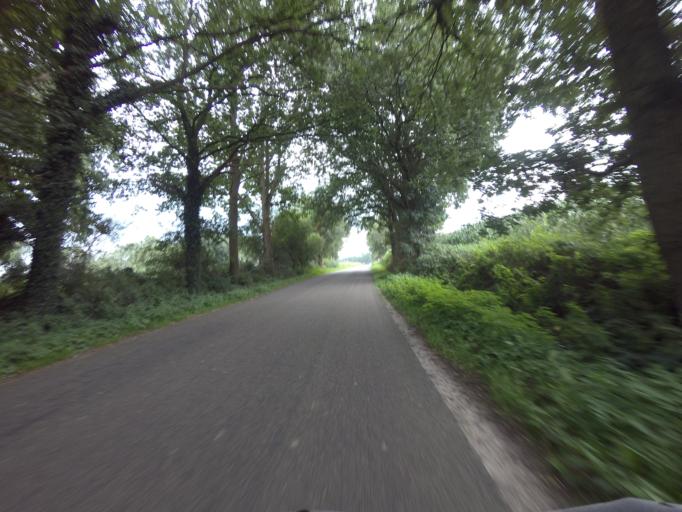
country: DE
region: Lower Saxony
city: Uelsen
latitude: 52.4596
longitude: 6.9135
